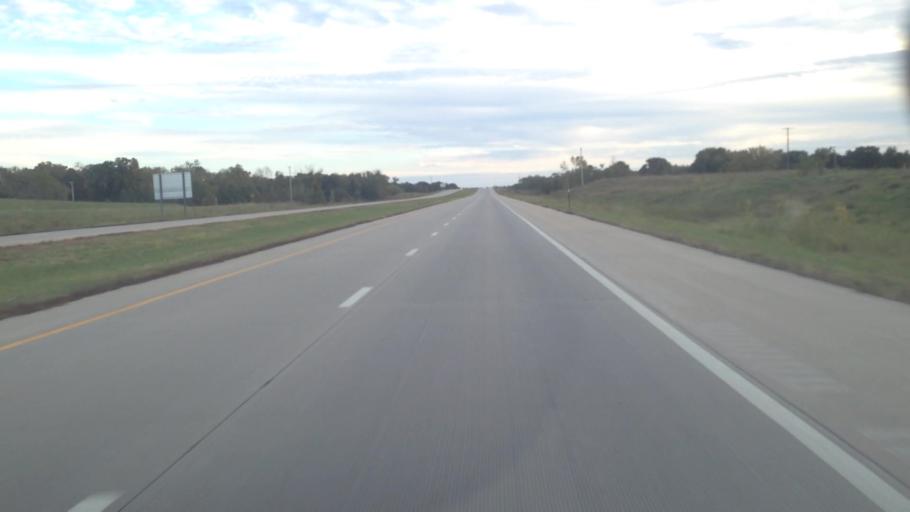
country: US
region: Kansas
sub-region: Douglas County
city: Baldwin City
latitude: 38.7703
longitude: -95.2687
